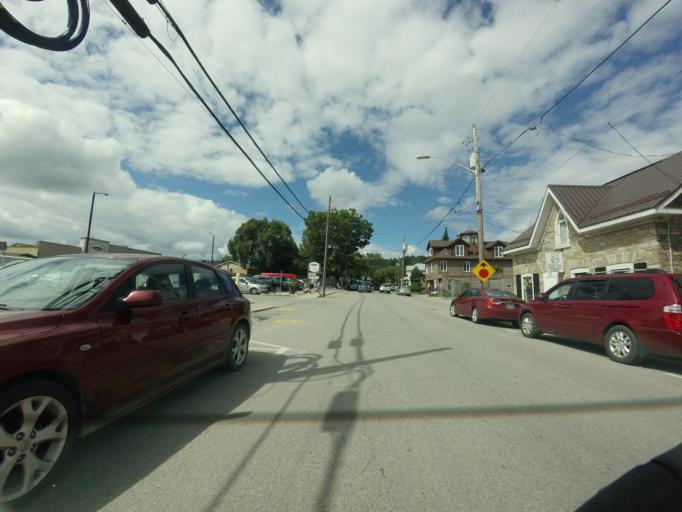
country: CA
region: Ontario
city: Perth
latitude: 44.6787
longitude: -76.3949
